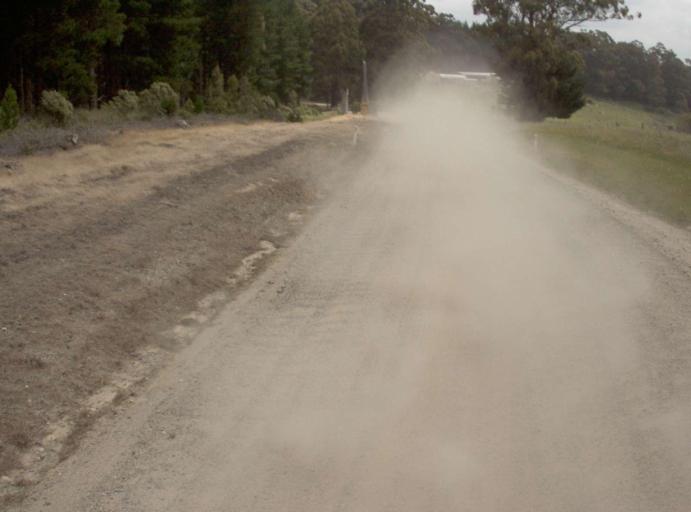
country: AU
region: Victoria
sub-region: Latrobe
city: Traralgon
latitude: -38.3787
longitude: 146.6706
